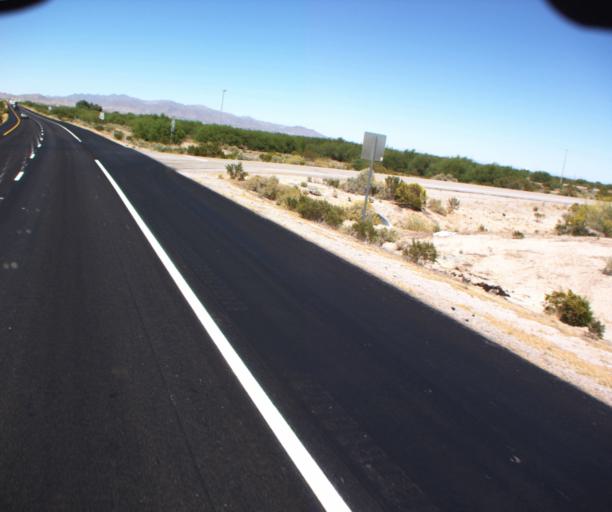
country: US
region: Arizona
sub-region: Maricopa County
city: Buckeye
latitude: 33.3181
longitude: -112.6229
